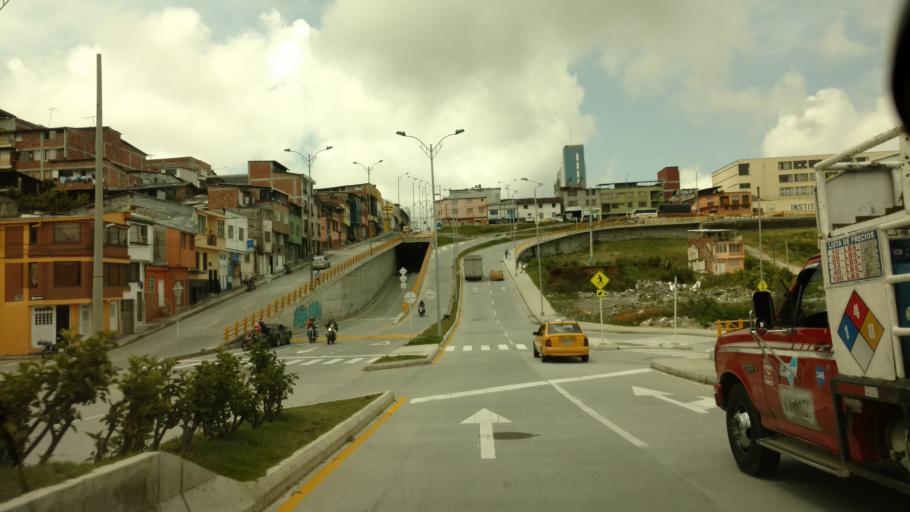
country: CO
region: Caldas
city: Manizales
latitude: 5.0708
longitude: -75.5116
